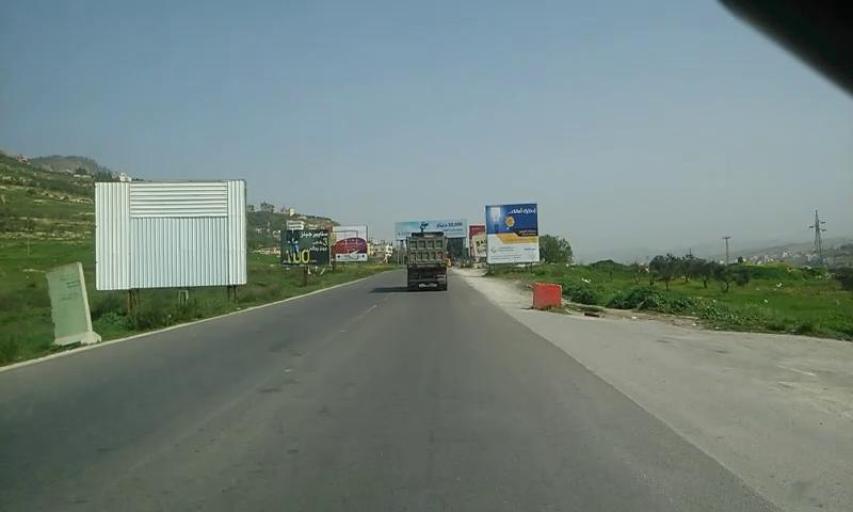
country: PS
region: West Bank
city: Kafr Qallil
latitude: 32.1792
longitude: 35.2743
